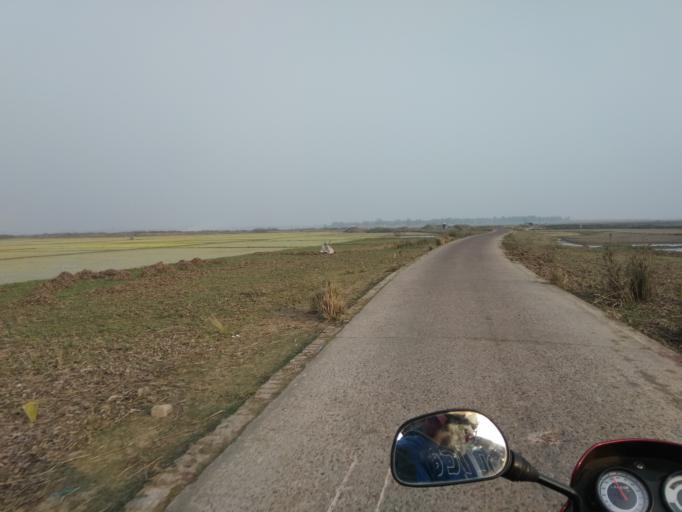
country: BD
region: Rajshahi
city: Ishurdi
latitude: 24.4845
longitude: 89.2180
